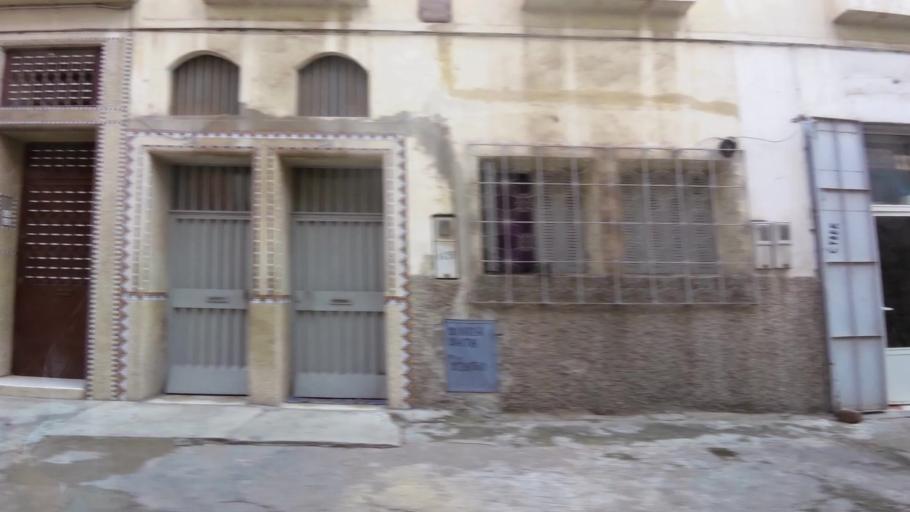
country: MA
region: Chaouia-Ouardigha
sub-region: Settat Province
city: Berrechid
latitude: 33.2676
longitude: -7.5747
